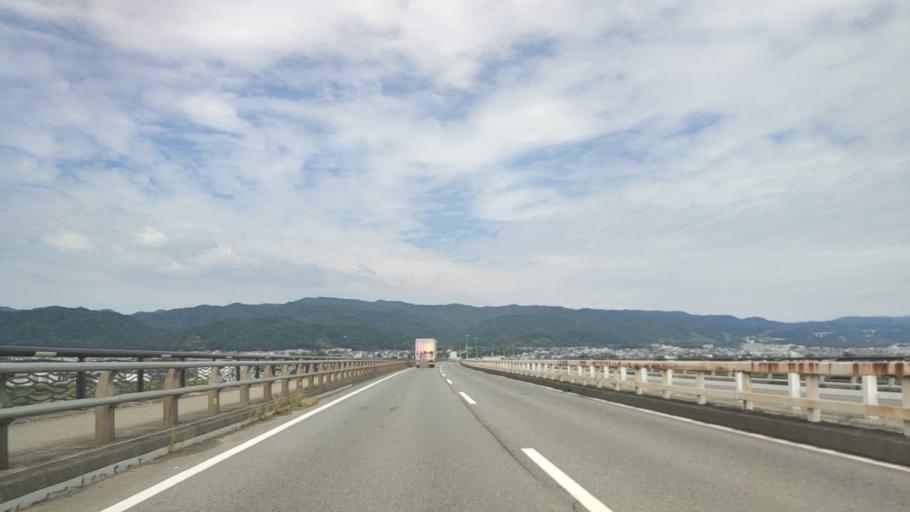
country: JP
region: Wakayama
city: Wakayama-shi
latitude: 34.2527
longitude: 135.2199
